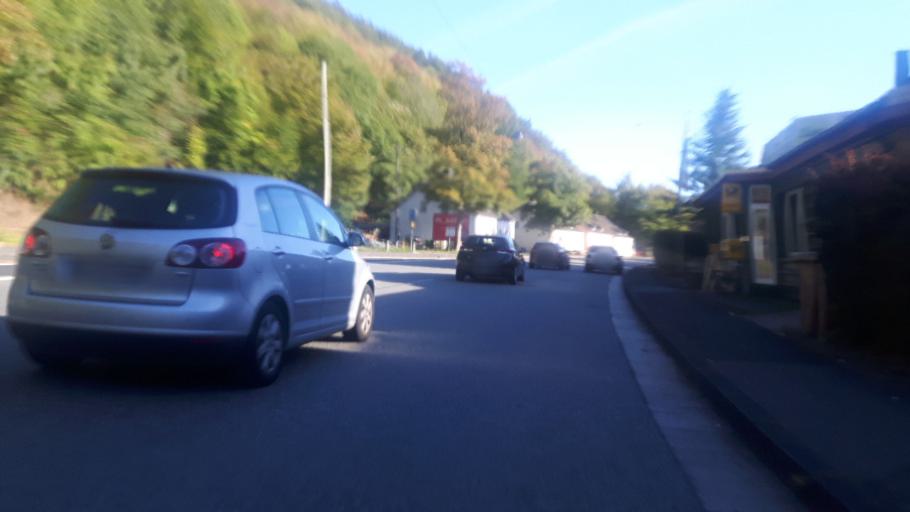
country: DE
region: Rheinland-Pfalz
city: Betzdorf
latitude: 50.8004
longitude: 7.8600
